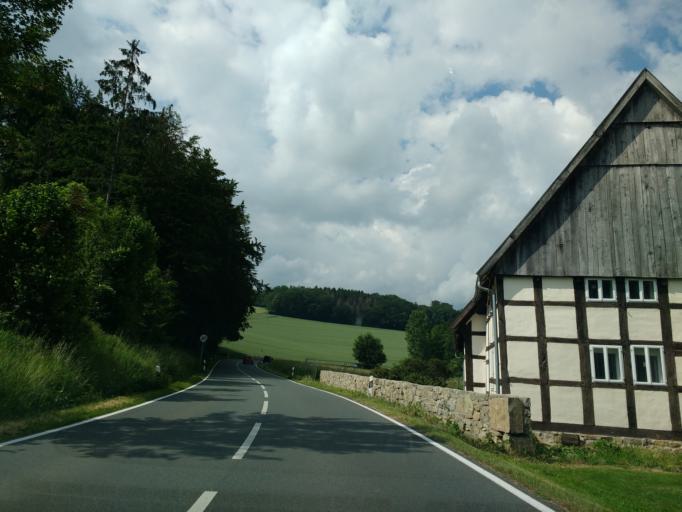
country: DE
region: North Rhine-Westphalia
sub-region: Regierungsbezirk Detmold
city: Lemgo
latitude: 52.0633
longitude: 8.9099
